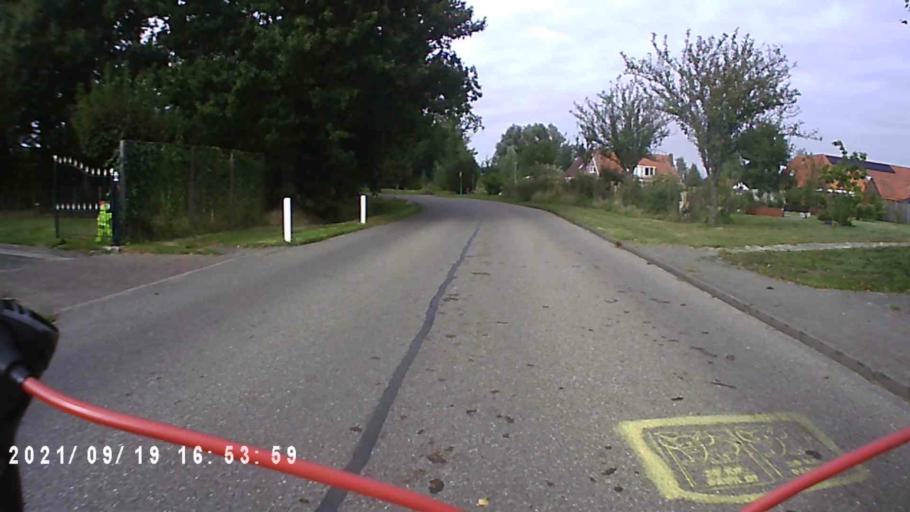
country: NL
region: Groningen
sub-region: Gemeente  Oldambt
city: Winschoten
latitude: 53.1854
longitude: 7.0784
